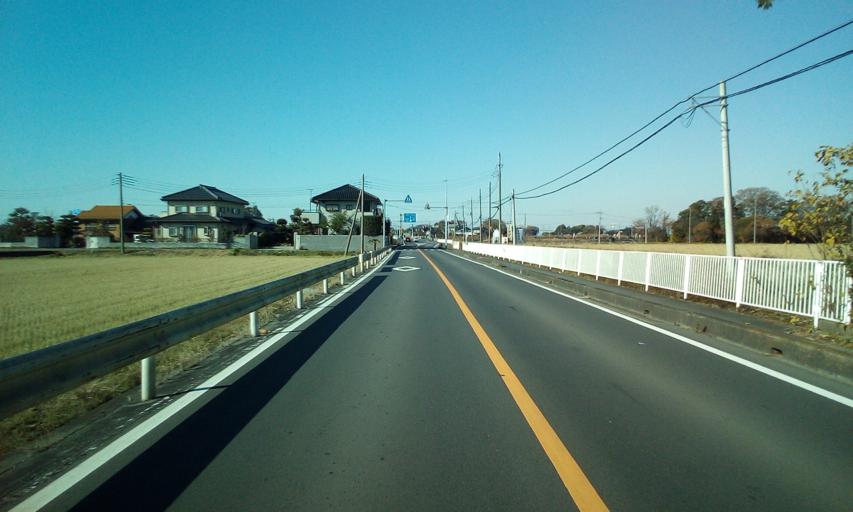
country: JP
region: Saitama
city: Sugito
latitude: 36.0518
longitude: 139.7749
